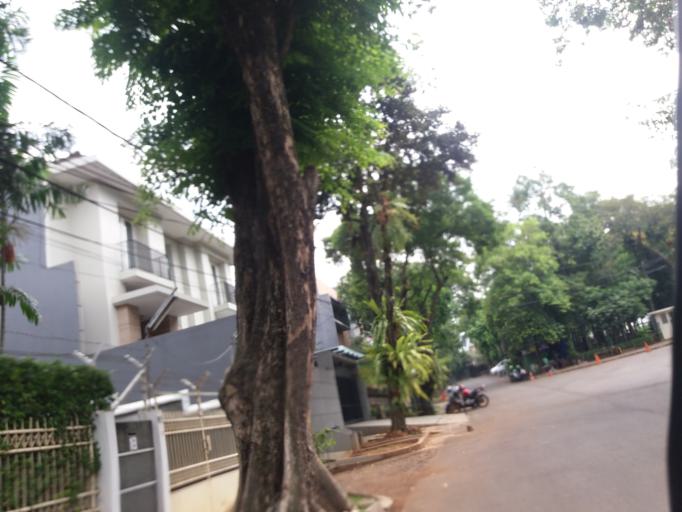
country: ID
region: Jakarta Raya
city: Jakarta
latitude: -6.2320
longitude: 106.8095
